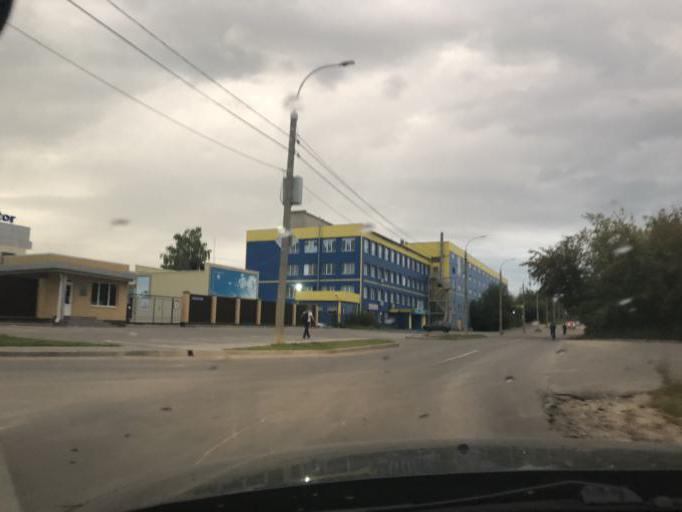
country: RU
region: Tula
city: Gorelki
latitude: 54.2256
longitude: 37.5983
